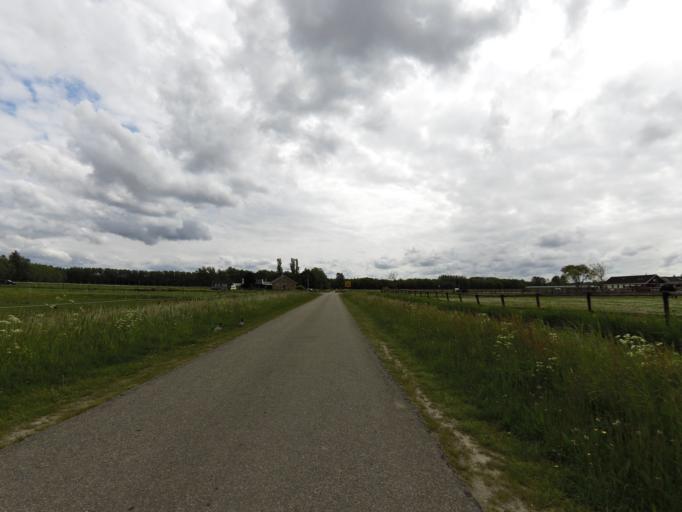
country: NL
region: South Holland
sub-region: Gemeente Hellevoetsluis
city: Nieuw-Helvoet
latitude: 51.8636
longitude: 4.0901
